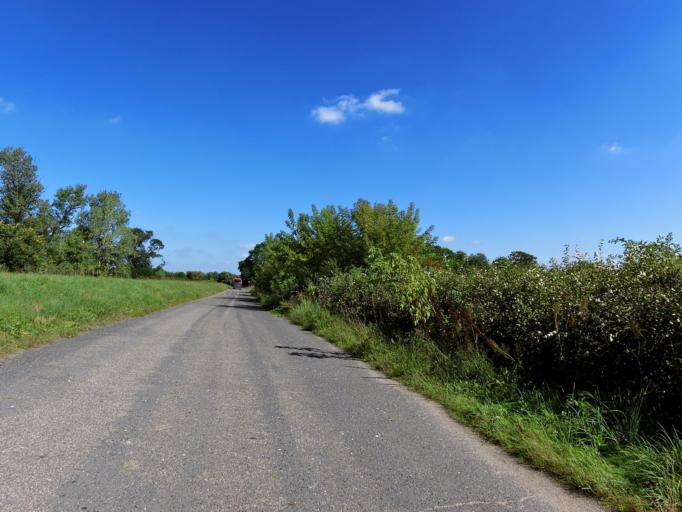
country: DE
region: Brandenburg
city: Muhlberg
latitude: 51.4257
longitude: 13.2256
